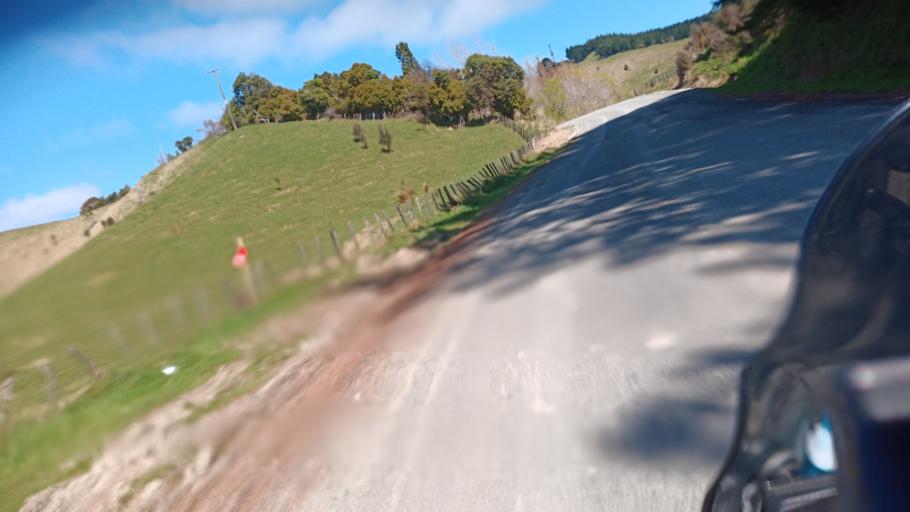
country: NZ
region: Gisborne
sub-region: Gisborne District
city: Gisborne
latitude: -38.8012
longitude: 177.7714
